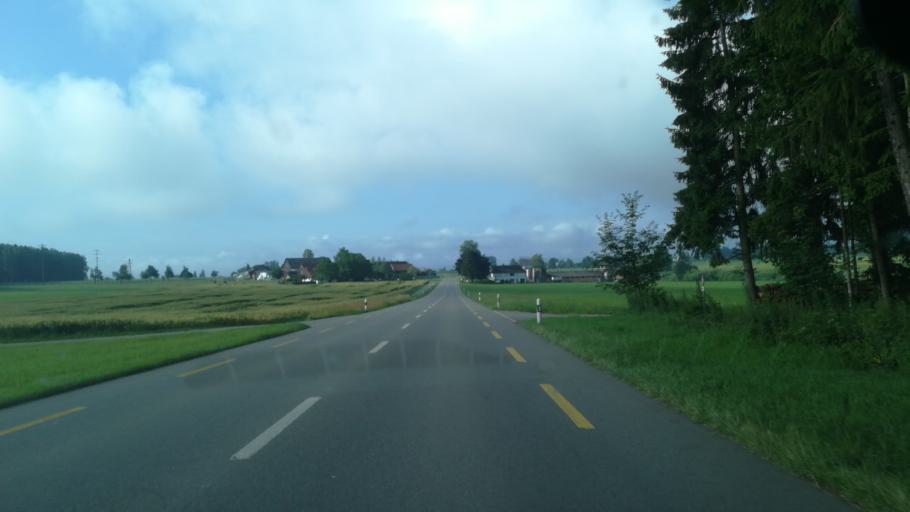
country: CH
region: Thurgau
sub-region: Weinfelden District
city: Berg
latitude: 47.5920
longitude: 9.1706
